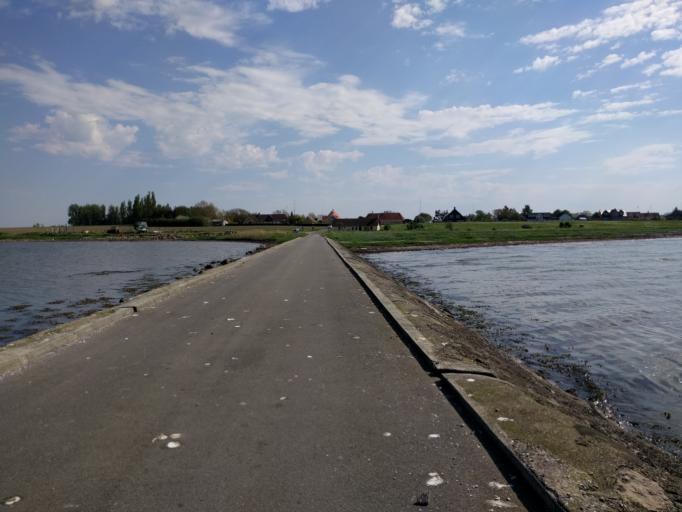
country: DK
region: South Denmark
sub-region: Kerteminde Kommune
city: Munkebo
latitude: 55.4849
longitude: 10.5977
